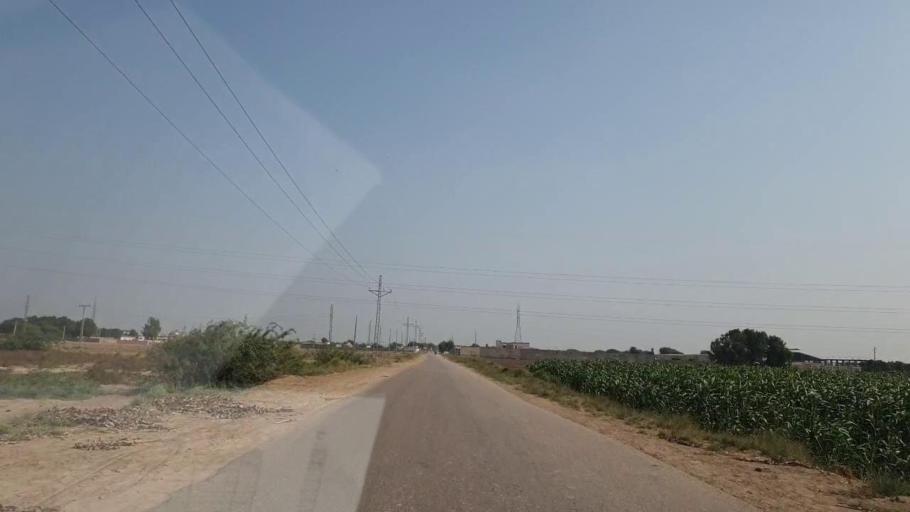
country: PK
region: Sindh
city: Matiari
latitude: 25.5048
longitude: 68.4289
